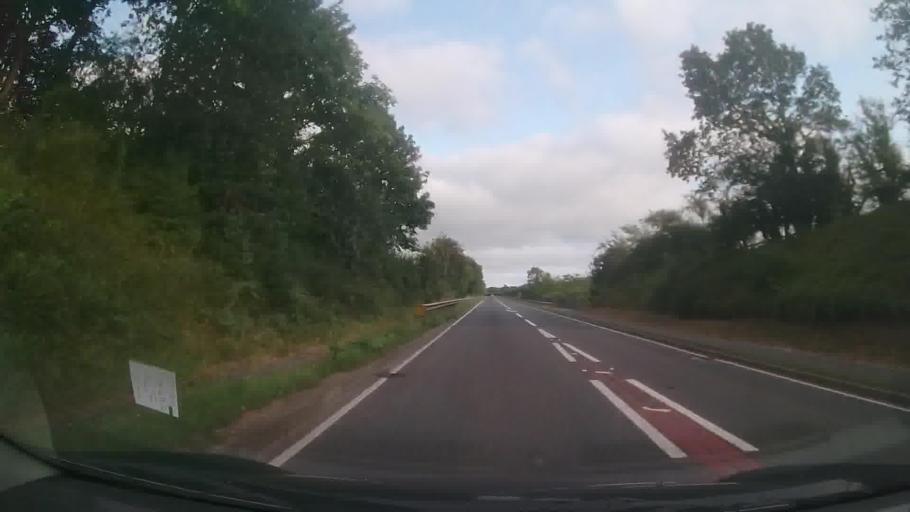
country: GB
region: Wales
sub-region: Pembrokeshire
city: Pembroke
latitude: 51.6913
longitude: -4.9160
